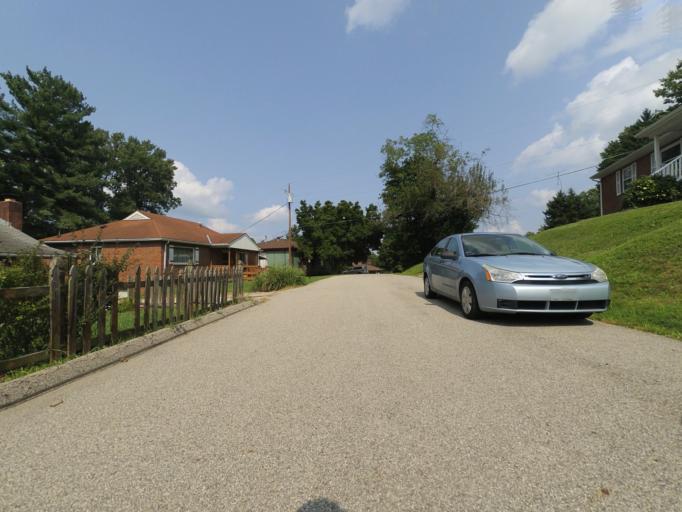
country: US
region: West Virginia
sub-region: Cabell County
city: Huntington
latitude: 38.3991
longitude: -82.4033
